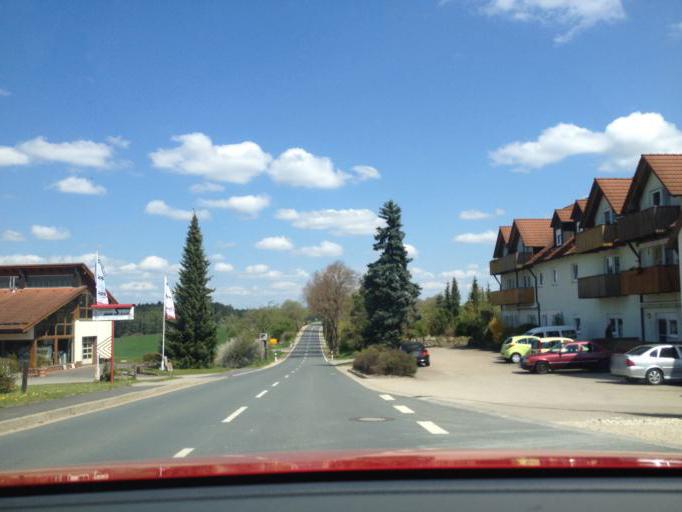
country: DE
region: Bavaria
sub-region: Upper Franconia
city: Pottenstein
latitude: 49.7119
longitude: 11.4427
